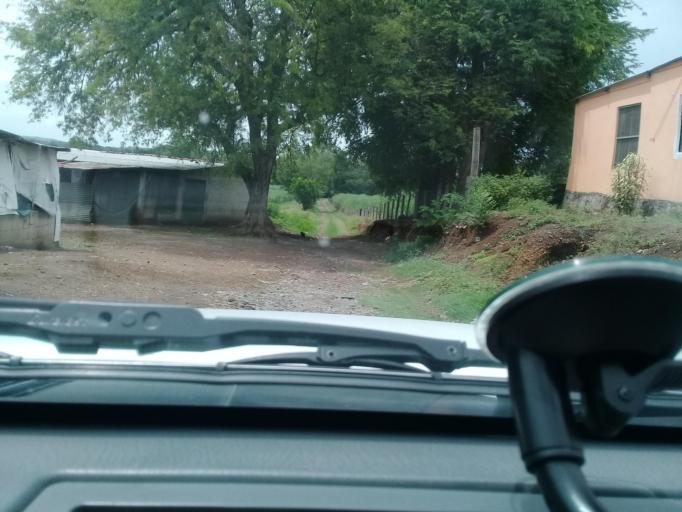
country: MX
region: Veracruz
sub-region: Paso de Ovejas
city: El Hatito
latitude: 19.2782
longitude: -96.3908
